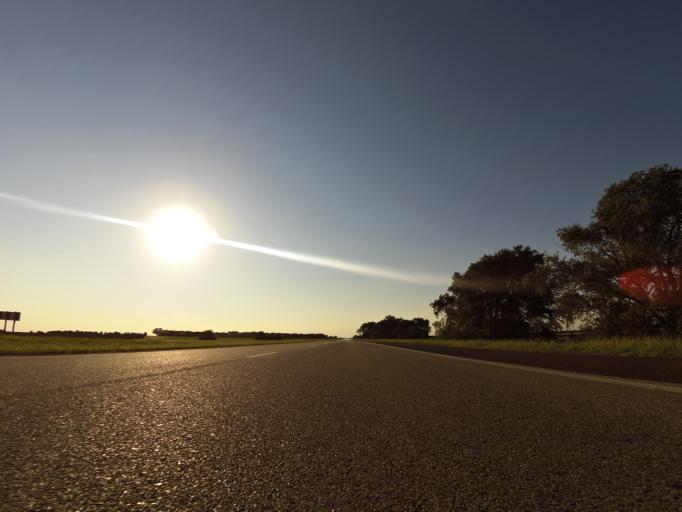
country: US
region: Kansas
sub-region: Reno County
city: Haven
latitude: 37.9120
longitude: -97.8127
